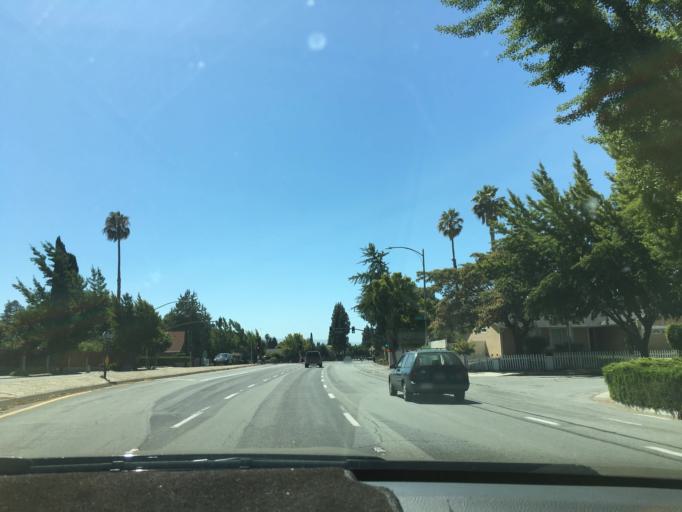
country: US
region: California
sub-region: Santa Clara County
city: Seven Trees
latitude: 37.2370
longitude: -121.8154
